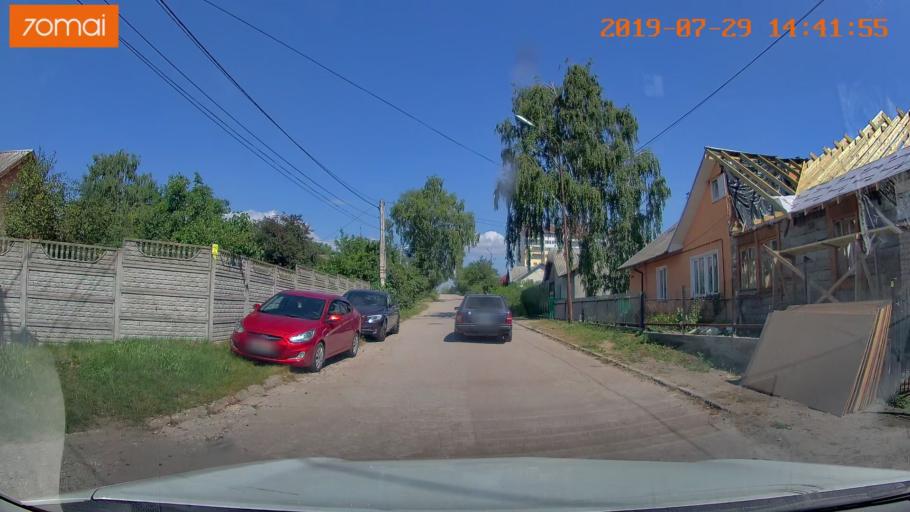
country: RU
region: Kaliningrad
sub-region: Gorod Kaliningrad
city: Baltiysk
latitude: 54.6578
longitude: 19.9011
